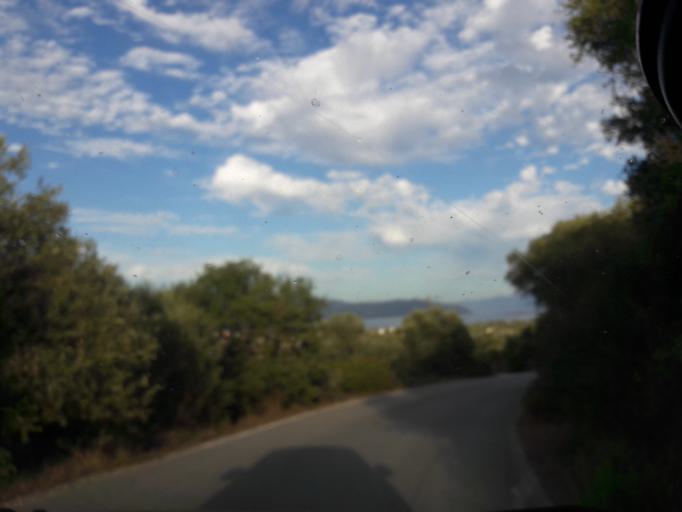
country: GR
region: Central Macedonia
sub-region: Nomos Chalkidikis
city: Nea Roda
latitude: 40.3325
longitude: 23.9107
